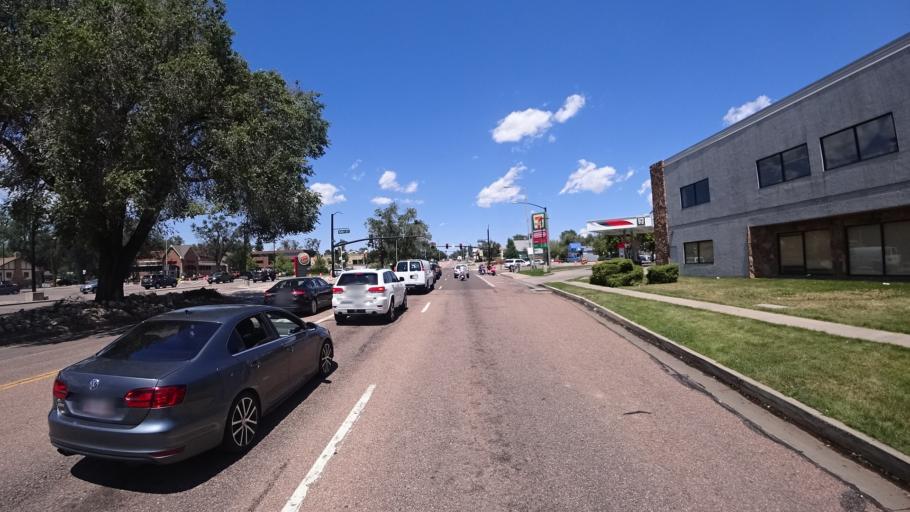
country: US
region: Colorado
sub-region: El Paso County
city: Colorado Springs
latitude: 38.8366
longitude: -104.7944
